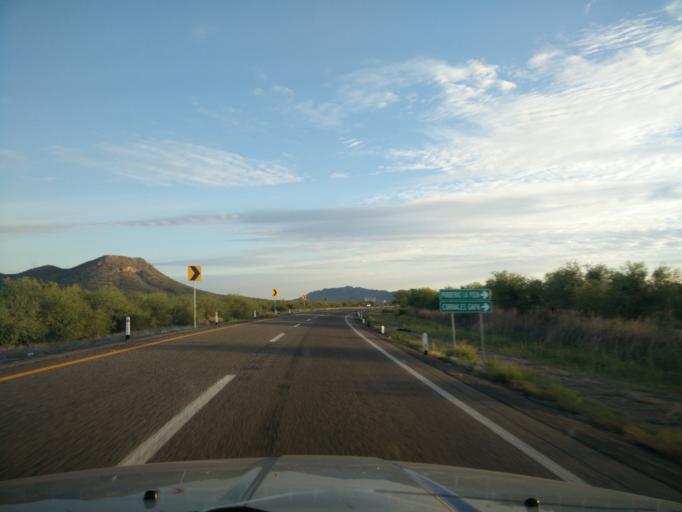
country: MX
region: Sonora
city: Hermosillo
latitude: 28.8752
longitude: -110.9585
